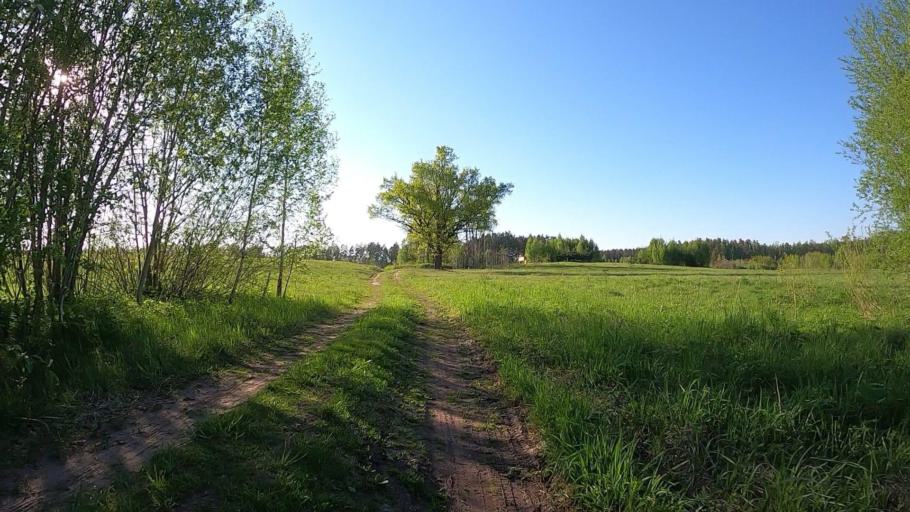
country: LV
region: Baldone
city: Baldone
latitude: 56.7722
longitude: 24.3283
